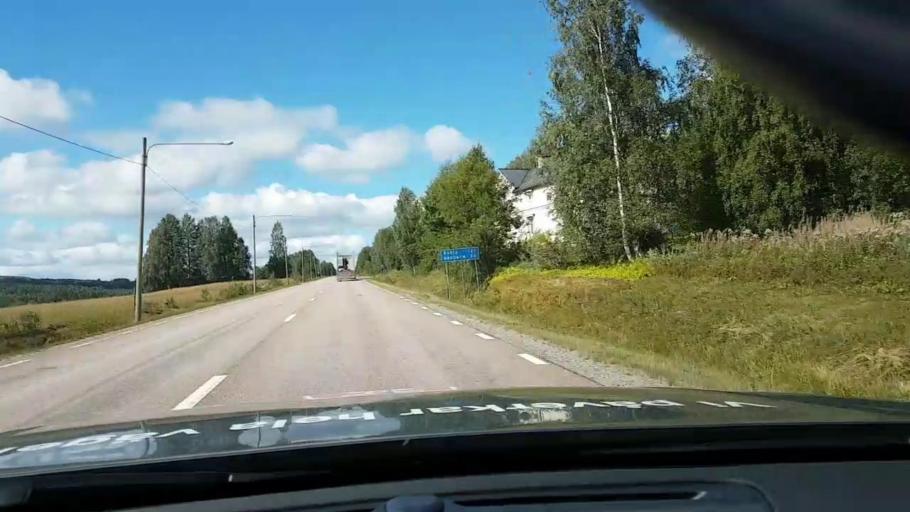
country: SE
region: Vaesternorrland
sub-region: OErnskoeldsviks Kommun
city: Bjasta
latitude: 63.3819
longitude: 18.4074
